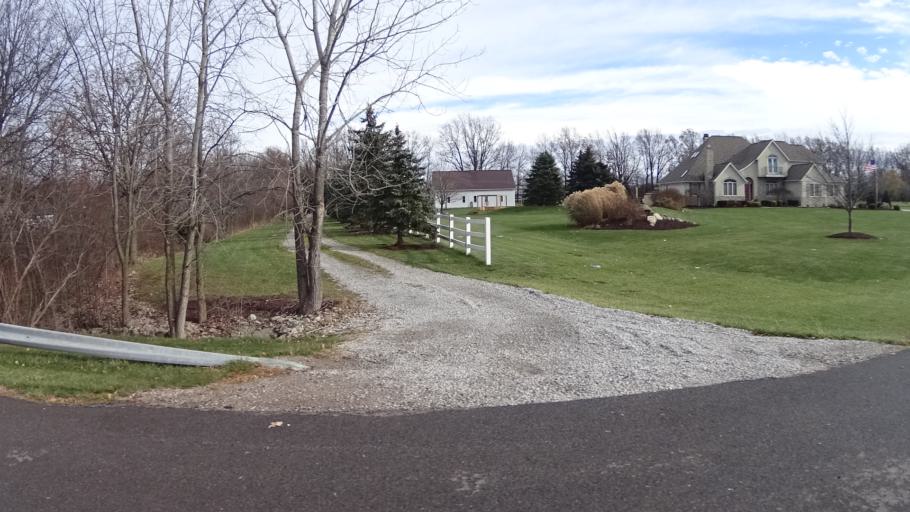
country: US
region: Ohio
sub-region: Lorain County
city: North Ridgeville
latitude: 41.3690
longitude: -82.0431
